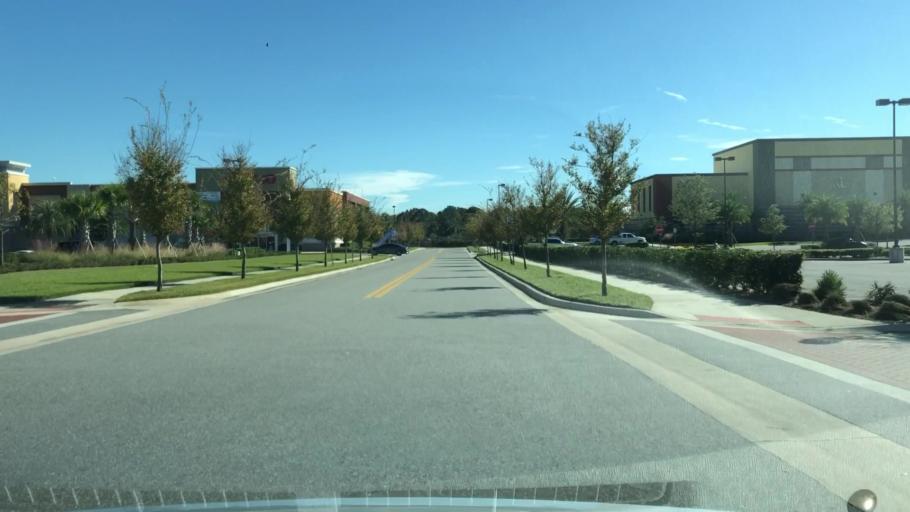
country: US
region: Florida
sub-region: Orange County
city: Conway
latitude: 28.4652
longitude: -81.3059
